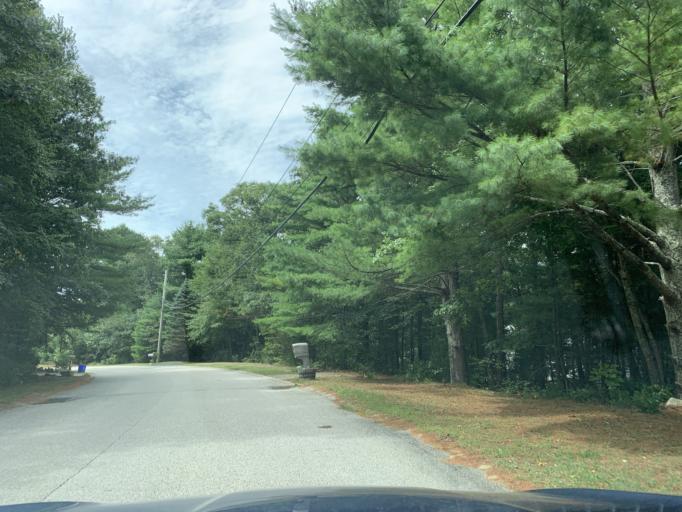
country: US
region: Rhode Island
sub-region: Washington County
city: Exeter
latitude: 41.5375
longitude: -71.6182
